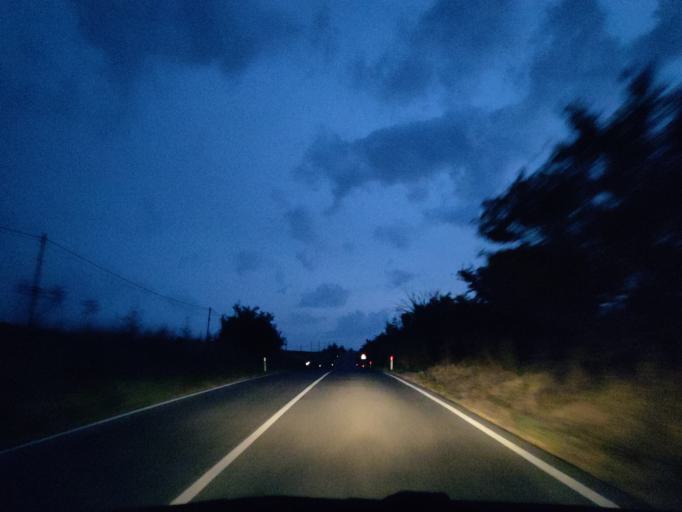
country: IT
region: Latium
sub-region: Provincia di Viterbo
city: Tarquinia
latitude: 42.2479
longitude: 11.8098
